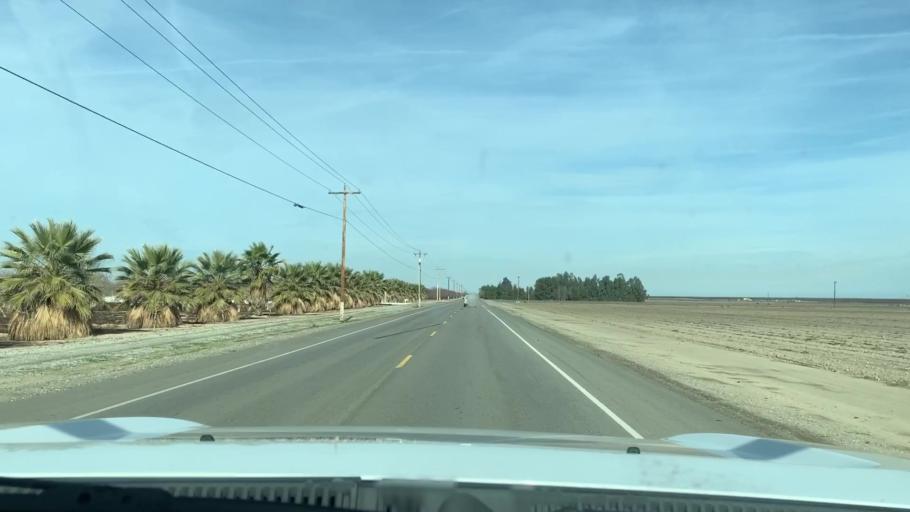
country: US
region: California
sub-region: Kern County
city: Buttonwillow
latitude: 35.5050
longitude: -119.4747
